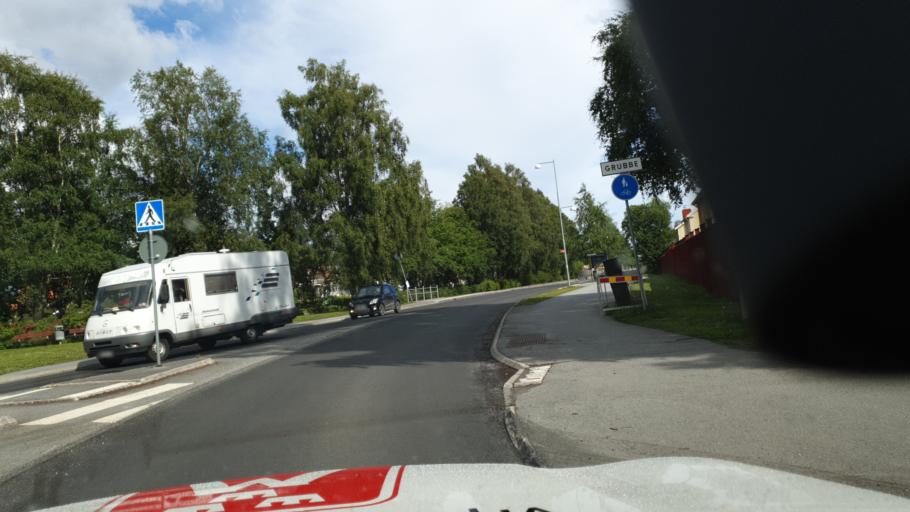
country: SE
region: Vaesterbotten
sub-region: Umea Kommun
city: Roback
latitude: 63.8352
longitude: 20.1972
